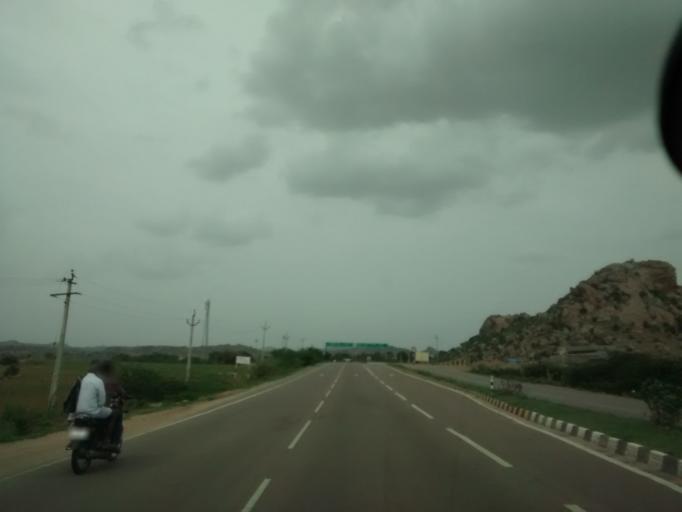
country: IN
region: Andhra Pradesh
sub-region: Kurnool
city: Ramapuram
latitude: 15.1666
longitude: 77.6778
